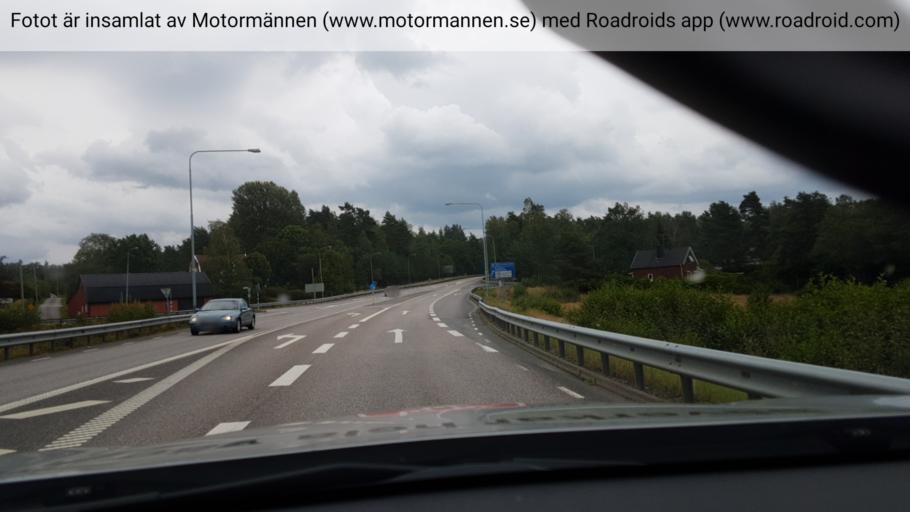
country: SE
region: Vaestra Goetaland
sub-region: Marks Kommun
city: Kinna
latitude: 57.4795
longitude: 12.7011
